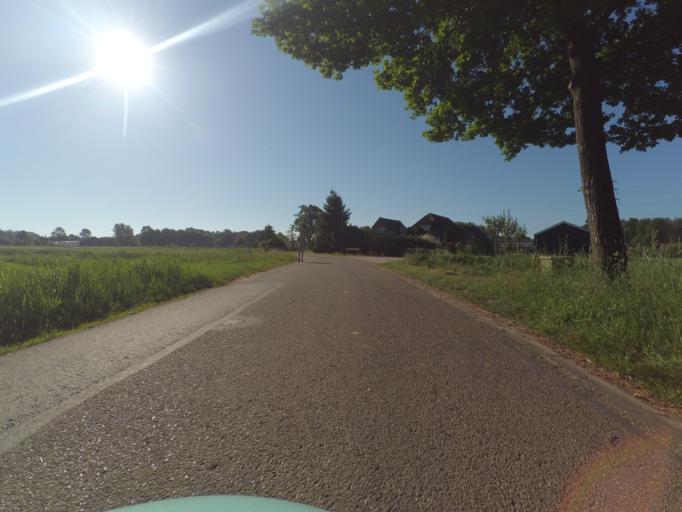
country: NL
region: Gelderland
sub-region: Gemeente Voorst
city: Voorst
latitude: 52.1720
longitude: 6.1094
